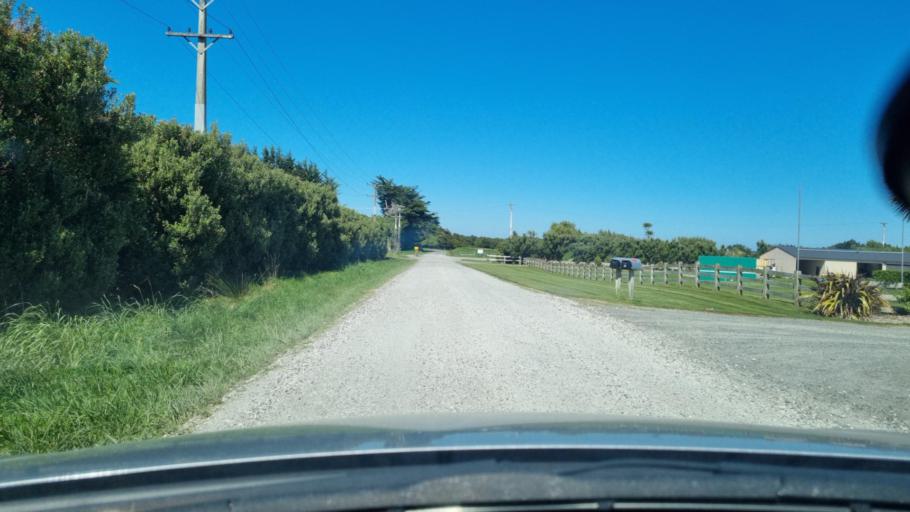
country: NZ
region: Southland
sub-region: Invercargill City
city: Invercargill
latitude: -46.4434
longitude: 168.2784
